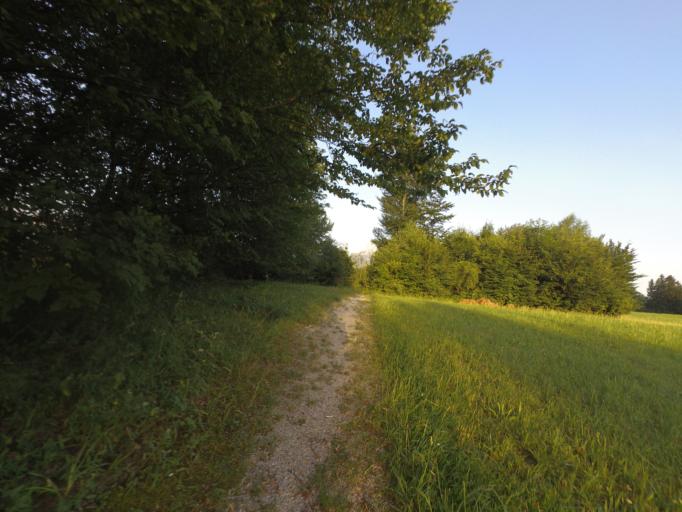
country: AT
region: Salzburg
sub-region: Politischer Bezirk Hallein
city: Puch bei Hallein
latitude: 47.7213
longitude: 13.0882
